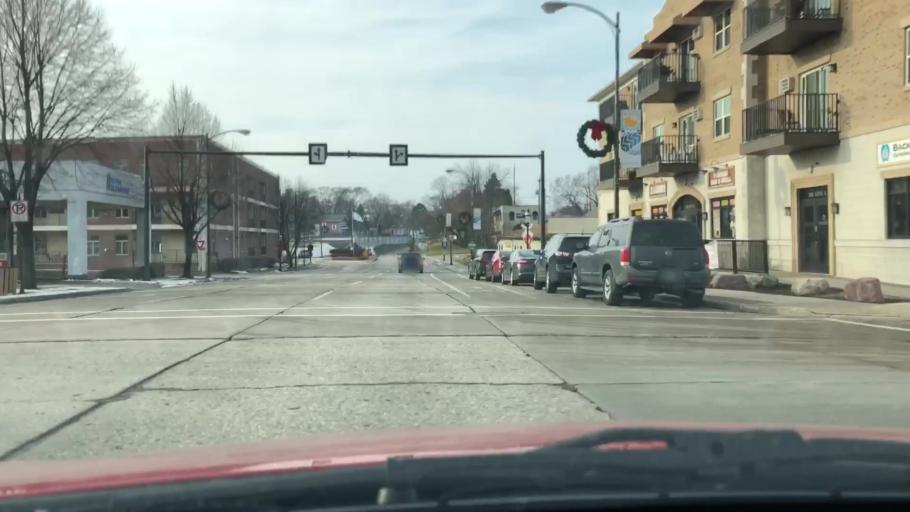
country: US
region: Wisconsin
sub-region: Brown County
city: De Pere
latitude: 44.4479
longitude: -88.0734
